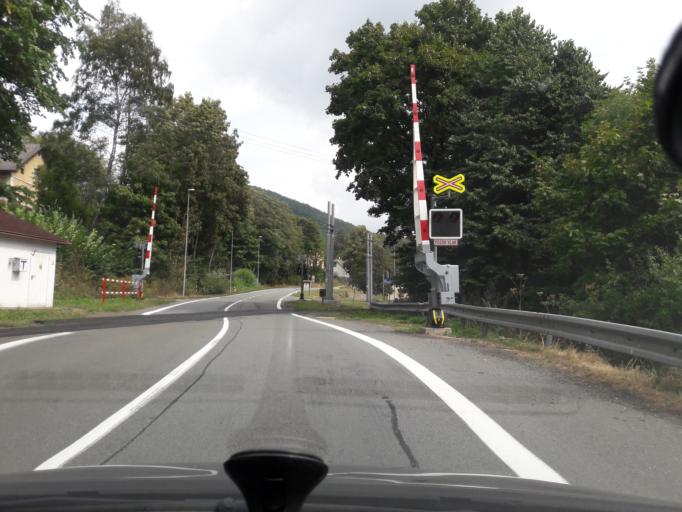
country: CZ
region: Olomoucky
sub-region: Okres Sumperk
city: Loucna nad Desnou
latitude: 50.0985
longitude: 17.1024
